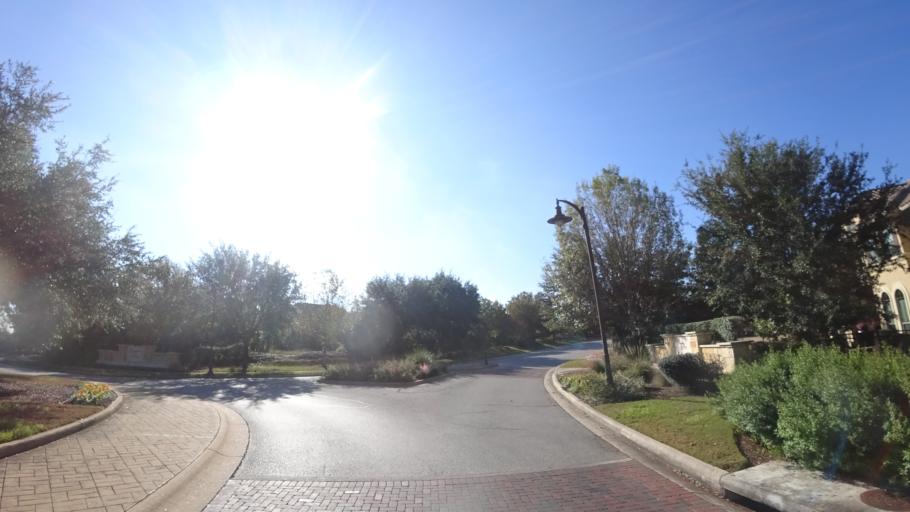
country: US
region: Texas
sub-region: Travis County
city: Bee Cave
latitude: 30.3556
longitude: -97.8926
